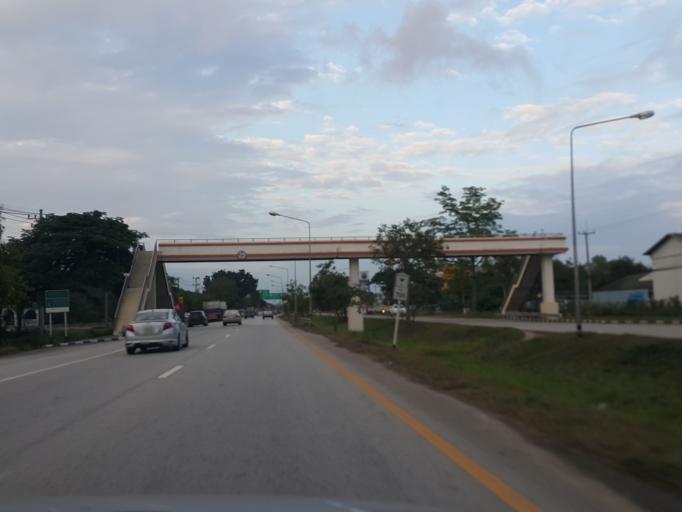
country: TH
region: Lampang
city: Lampang
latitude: 18.2602
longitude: 99.4635
